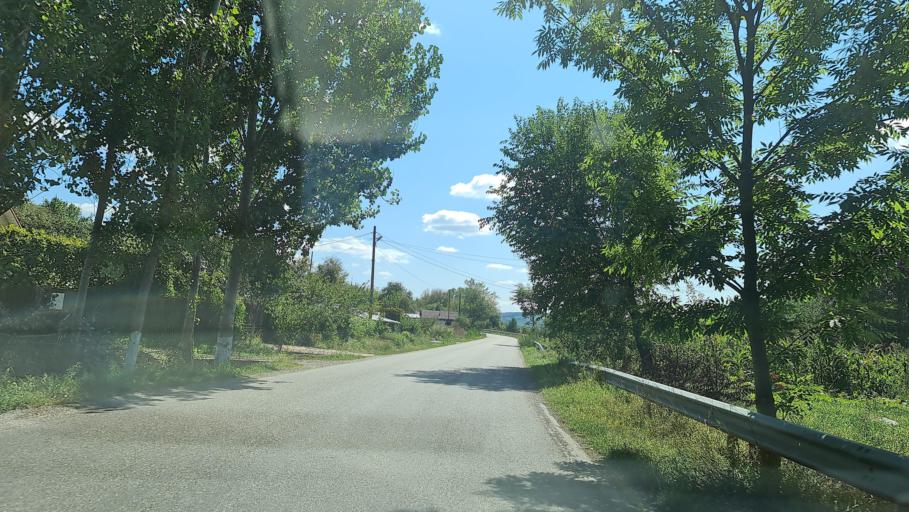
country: RO
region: Bacau
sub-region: Comuna Beresti-Tazlau
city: Beresti-Tazlau
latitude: 46.4981
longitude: 26.6815
